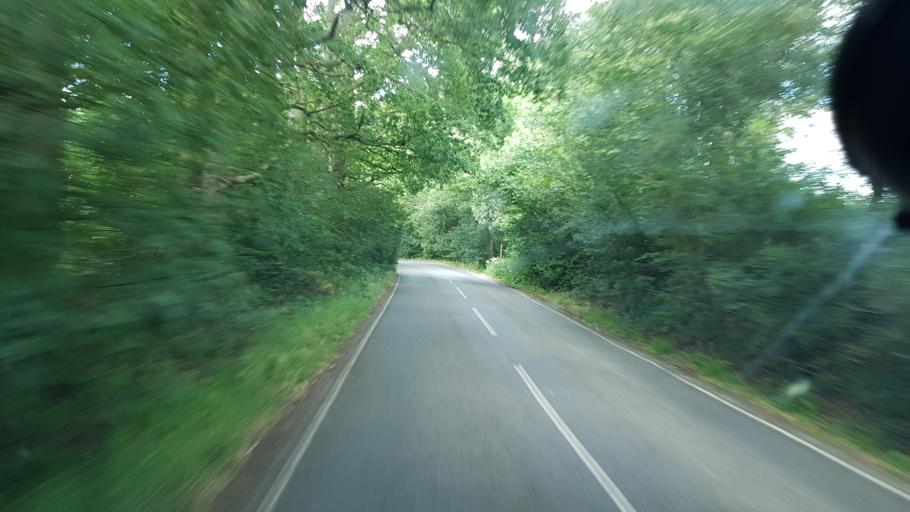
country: GB
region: England
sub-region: West Sussex
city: Rudgwick
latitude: 51.0761
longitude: -0.4529
